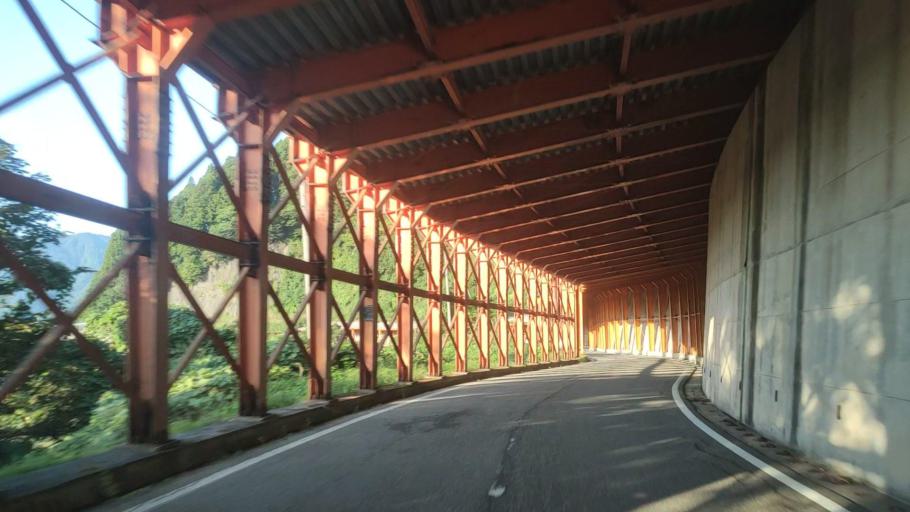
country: JP
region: Toyama
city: Nanto-shi
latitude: 36.5046
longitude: 137.0213
